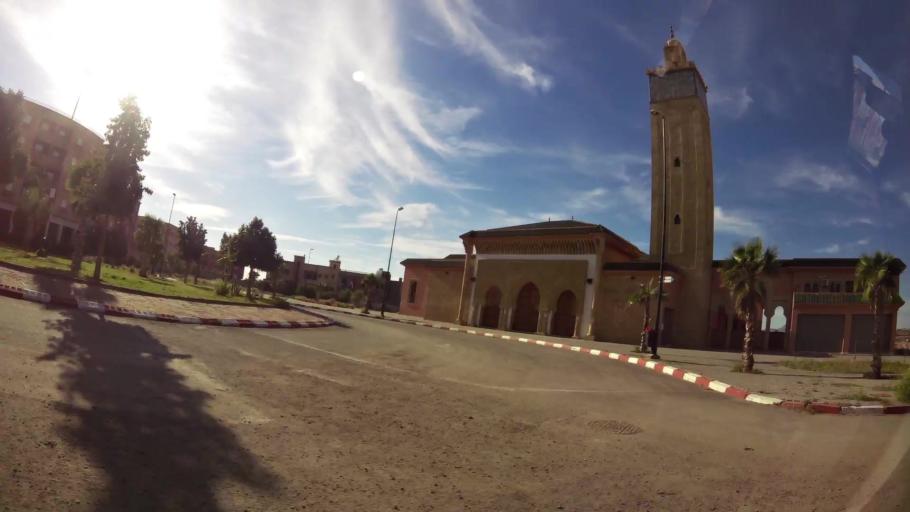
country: MA
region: Marrakech-Tensift-Al Haouz
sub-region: Marrakech
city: Marrakesh
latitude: 31.6898
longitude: -8.0685
